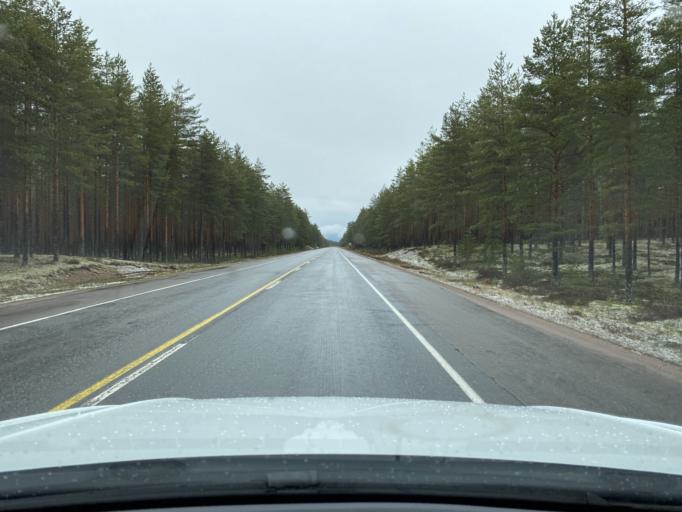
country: FI
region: Satakunta
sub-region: Pori
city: Vampula
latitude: 60.9694
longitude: 22.6811
